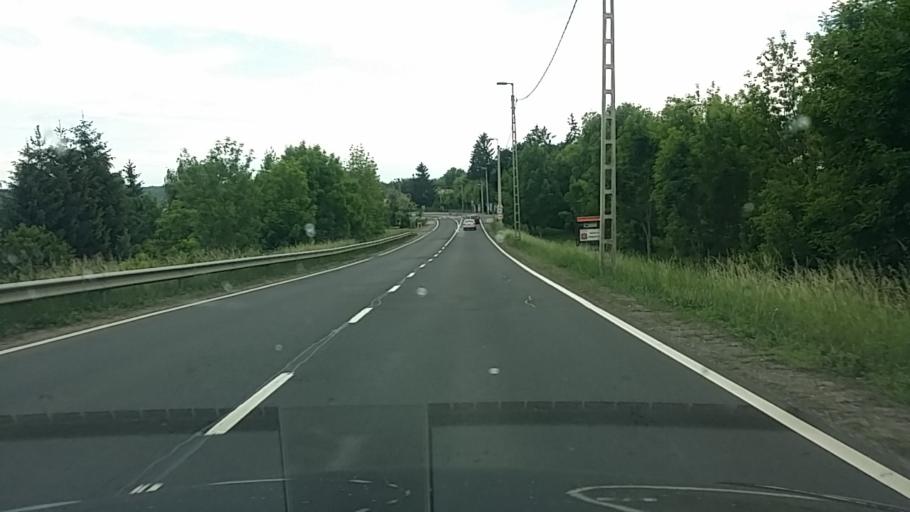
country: HU
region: Nograd
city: Nagyoroszi
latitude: 47.9773
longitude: 19.1180
